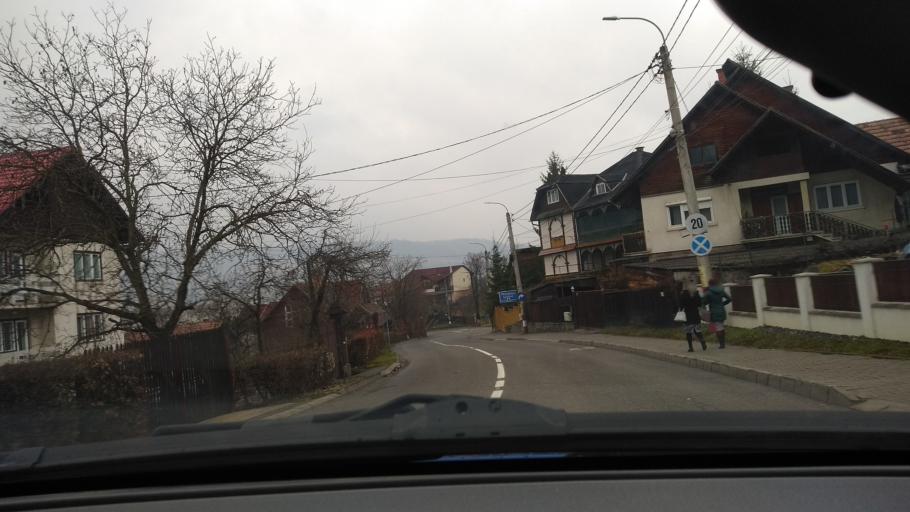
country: RO
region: Mures
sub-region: Oras Sovata
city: Sovata
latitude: 46.5965
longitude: 25.0756
